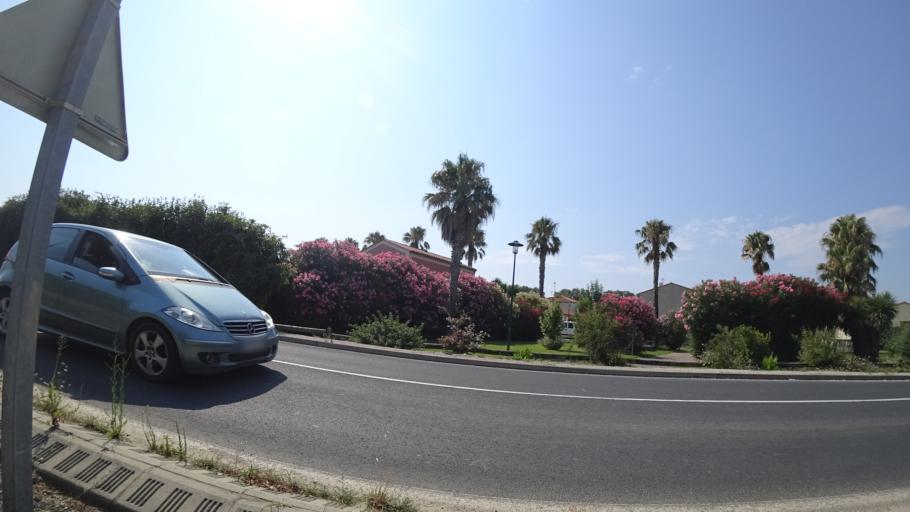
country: FR
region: Languedoc-Roussillon
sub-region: Departement des Pyrenees-Orientales
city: Bompas
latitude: 42.7230
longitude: 2.9385
